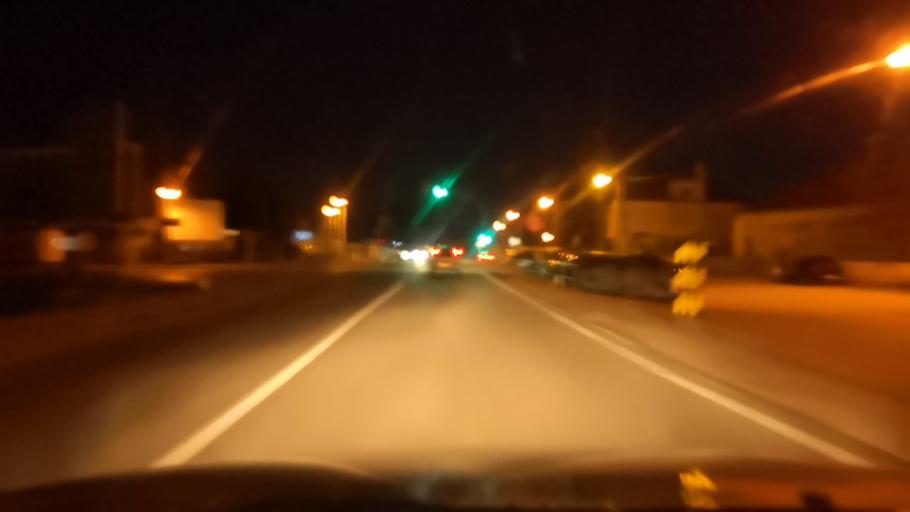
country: PT
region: Setubal
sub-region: Palmela
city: Palmela
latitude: 38.5668
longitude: -8.8879
